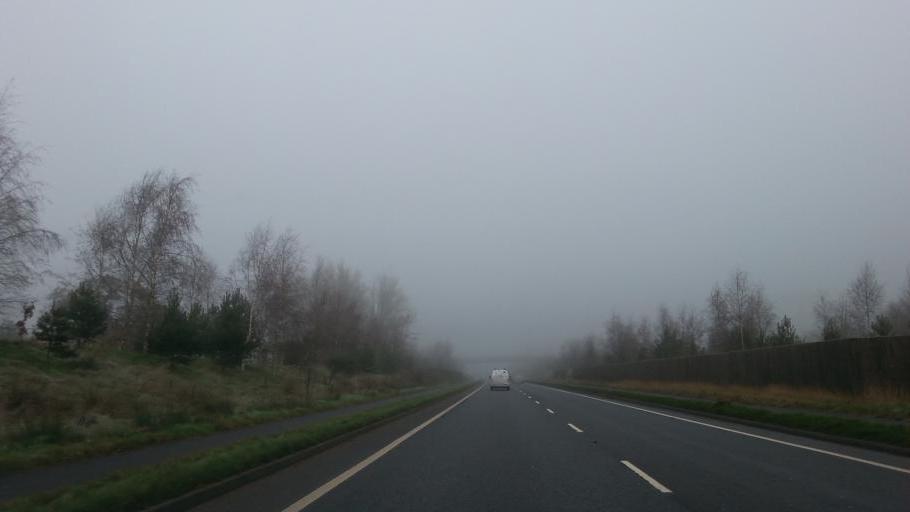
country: GB
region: England
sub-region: Cheshire East
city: Alderley Edge
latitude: 53.2767
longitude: -2.2421
